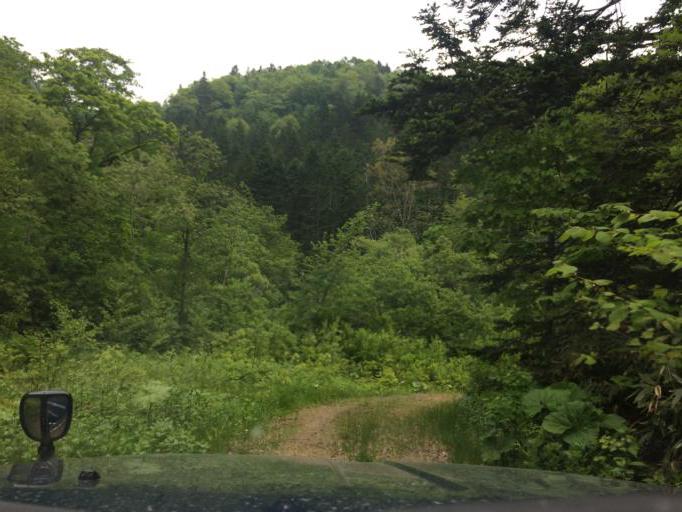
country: JP
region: Hokkaido
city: Niseko Town
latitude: 42.6349
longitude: 140.5735
